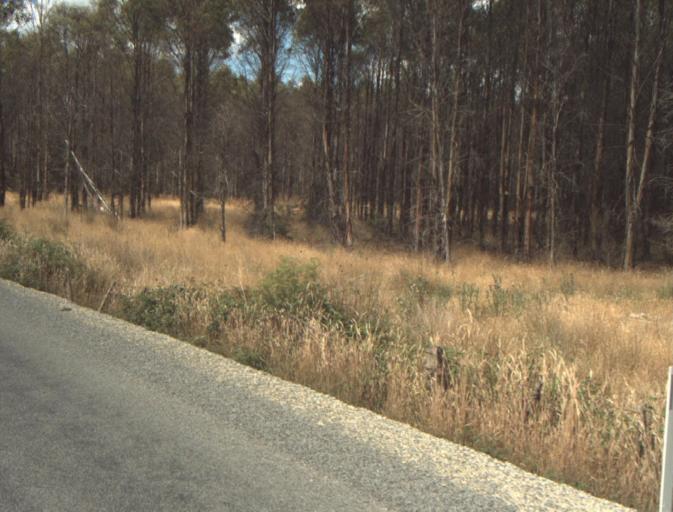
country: AU
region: Tasmania
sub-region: Launceston
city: Mayfield
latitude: -41.2141
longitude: 147.1907
